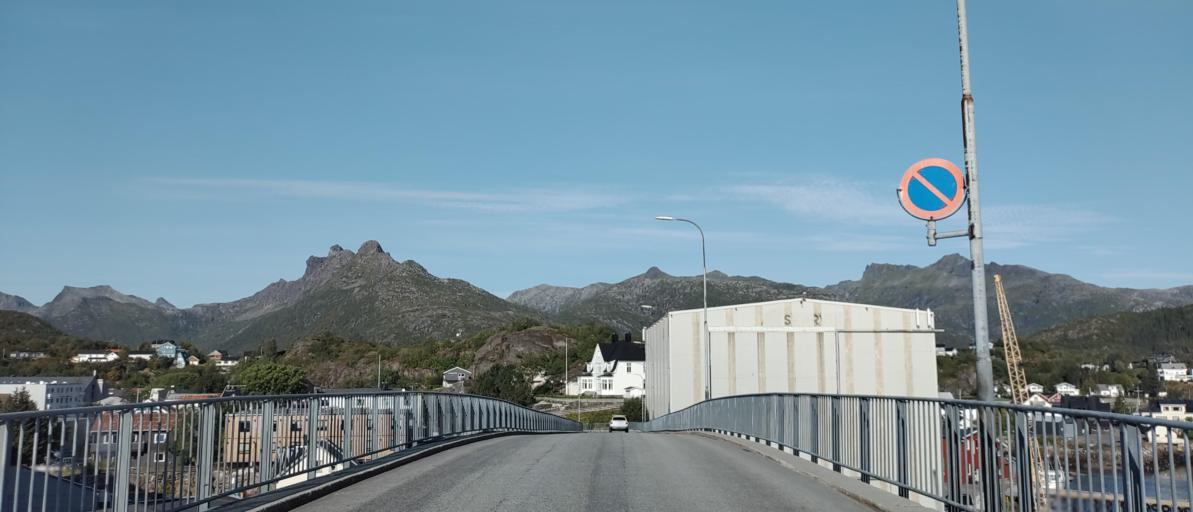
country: NO
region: Nordland
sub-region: Vagan
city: Svolvaer
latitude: 68.2361
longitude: 14.5756
